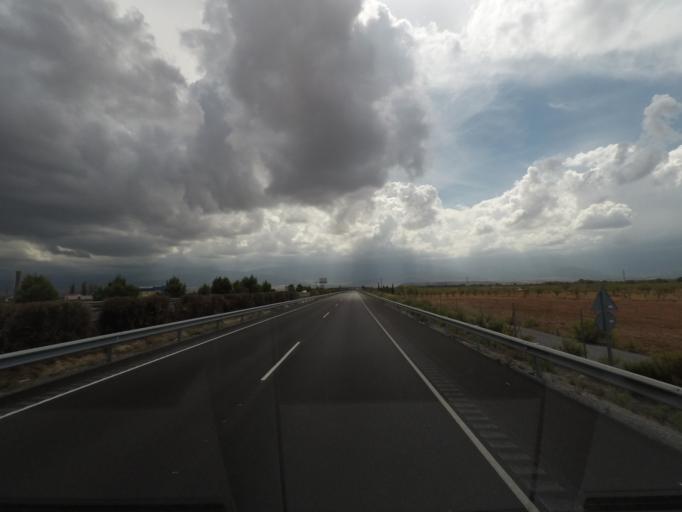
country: ES
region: Andalusia
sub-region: Provincia de Granada
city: Albunan
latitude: 37.2548
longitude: -3.0815
